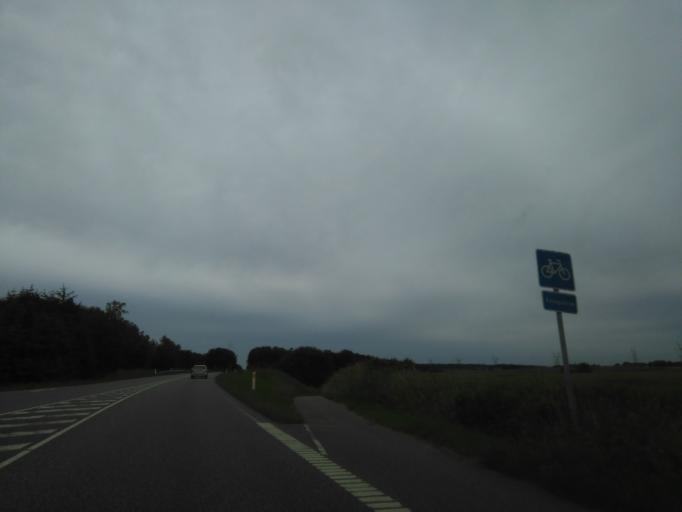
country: DK
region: Central Jutland
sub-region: Horsens Kommune
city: Horsens
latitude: 55.9162
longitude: 9.9238
